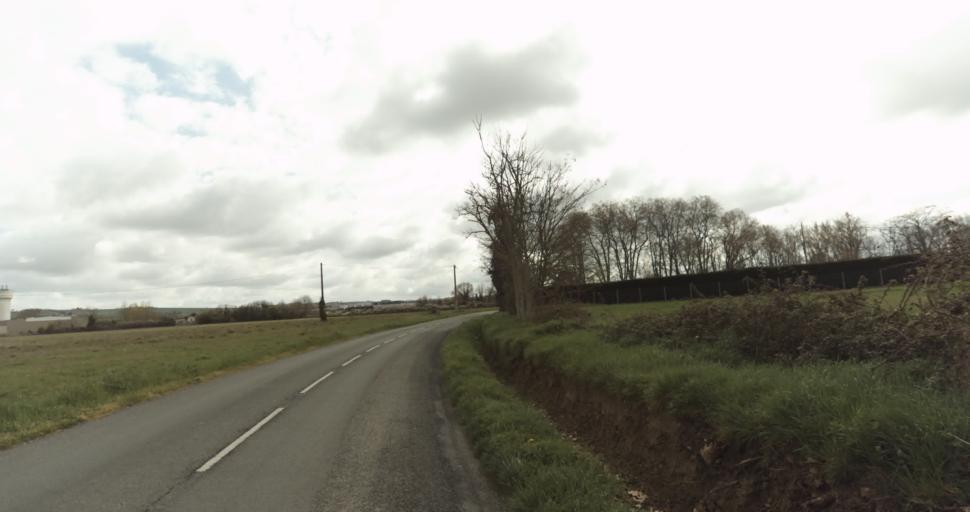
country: FR
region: Midi-Pyrenees
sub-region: Departement de la Haute-Garonne
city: Auterive
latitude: 43.3576
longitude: 1.4570
